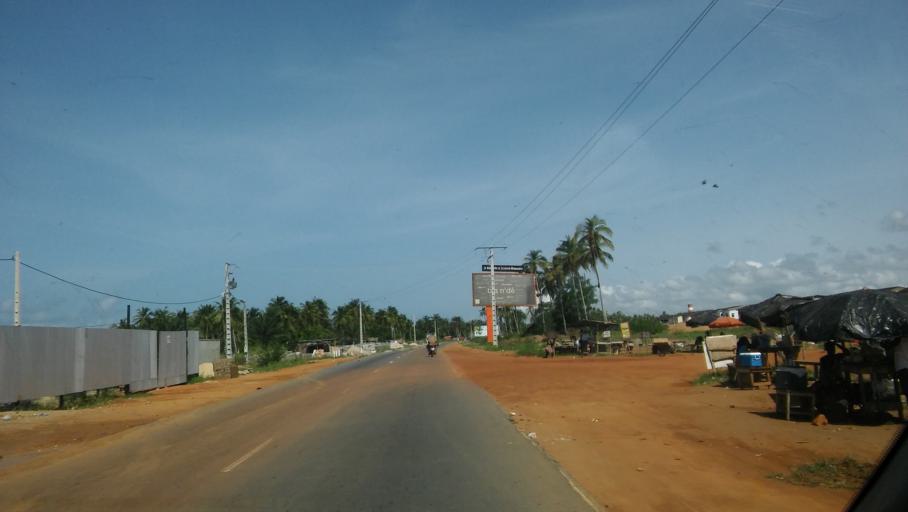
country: CI
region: Sud-Comoe
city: Grand-Bassam
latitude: 5.2128
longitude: -3.7836
